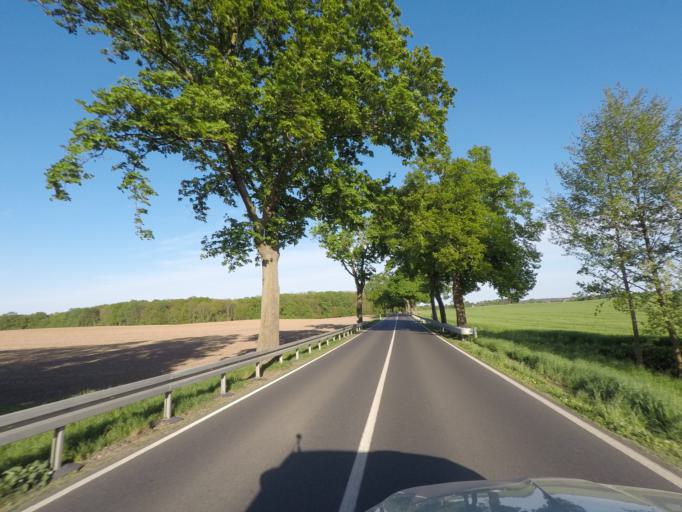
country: DE
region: Brandenburg
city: Hohenfinow
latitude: 52.8160
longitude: 13.9065
